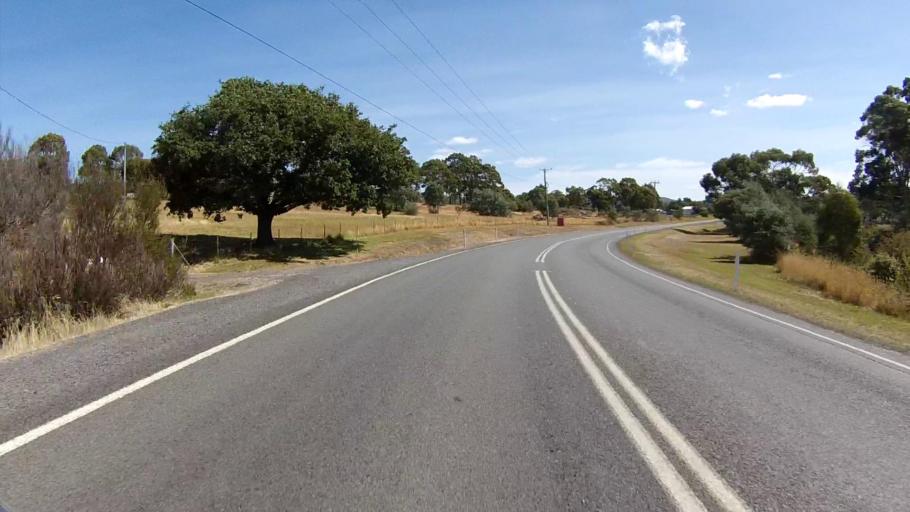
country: AU
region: Tasmania
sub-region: Sorell
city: Sorell
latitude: -42.6105
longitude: 147.7340
